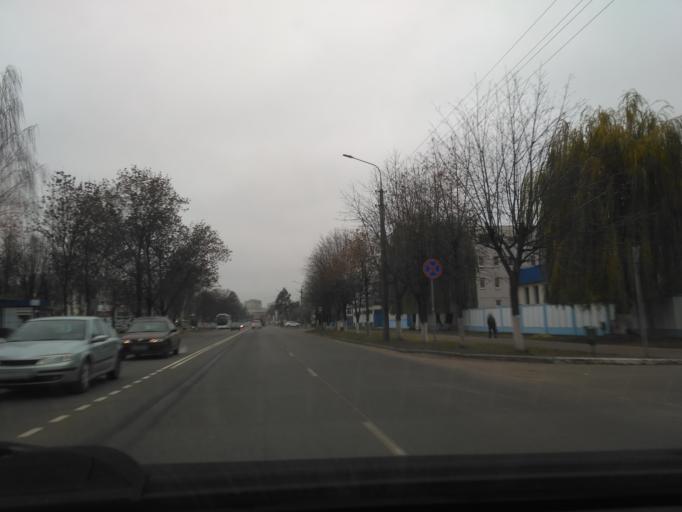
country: BY
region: Minsk
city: Horad Barysaw
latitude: 54.2072
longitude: 28.4953
